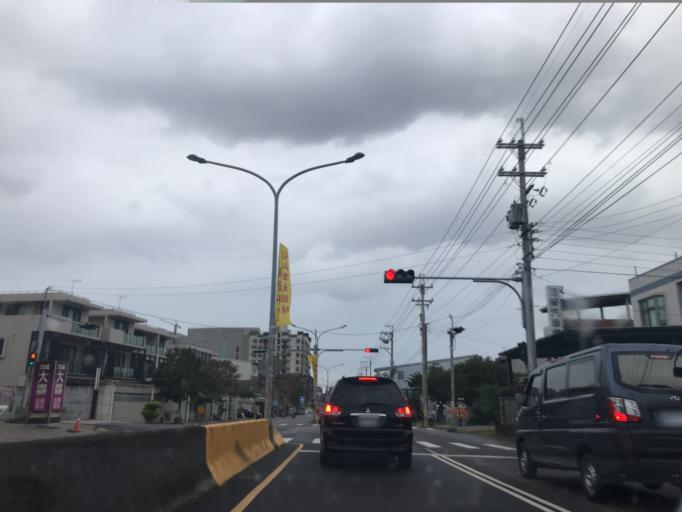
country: TW
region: Taiwan
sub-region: Hsinchu
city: Zhubei
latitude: 24.8320
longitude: 121.0314
